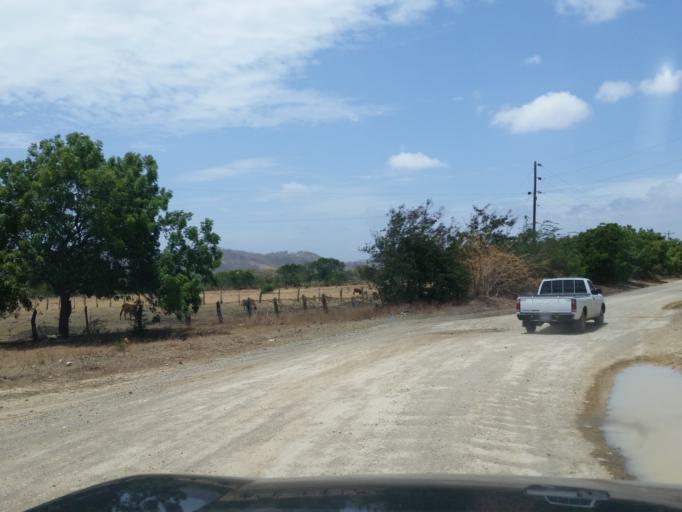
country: NI
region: Rivas
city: Tola
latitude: 11.4669
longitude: -86.0872
